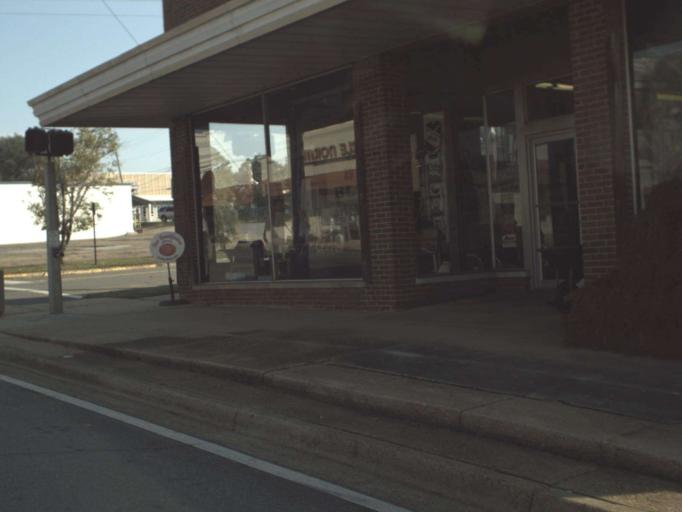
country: US
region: Florida
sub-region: Holmes County
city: Bonifay
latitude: 30.7918
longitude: -85.6796
